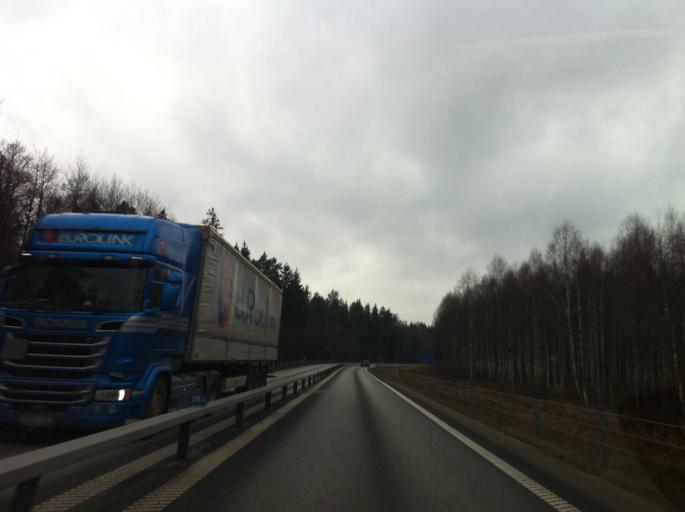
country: SE
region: Joenkoeping
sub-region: Vetlanda Kommun
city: Vetlanda
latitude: 57.4168
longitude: 15.1033
